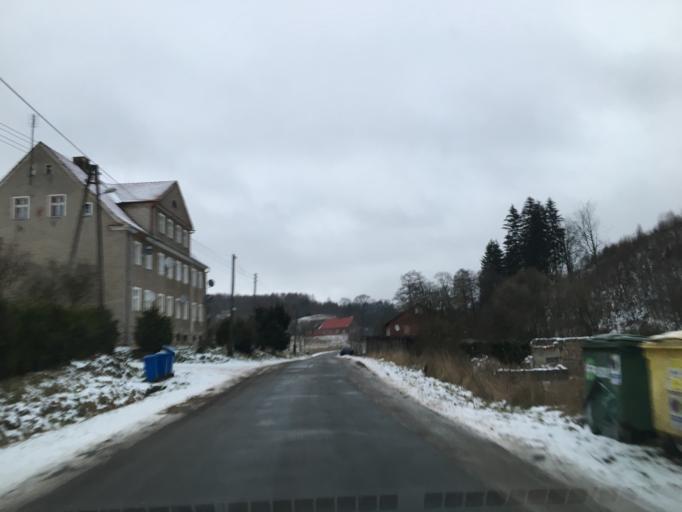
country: CZ
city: Radvanice
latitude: 50.6271
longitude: 16.0360
